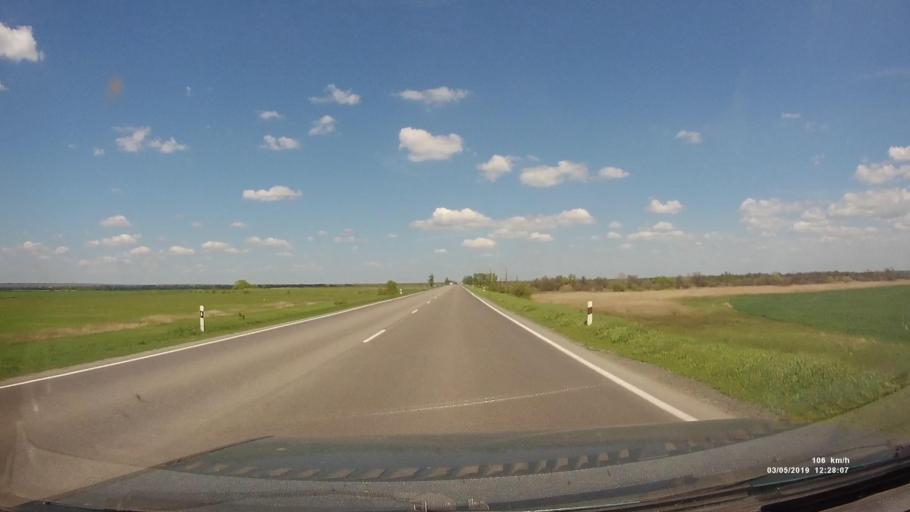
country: RU
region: Rostov
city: Semikarakorsk
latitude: 47.4687
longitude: 40.7258
